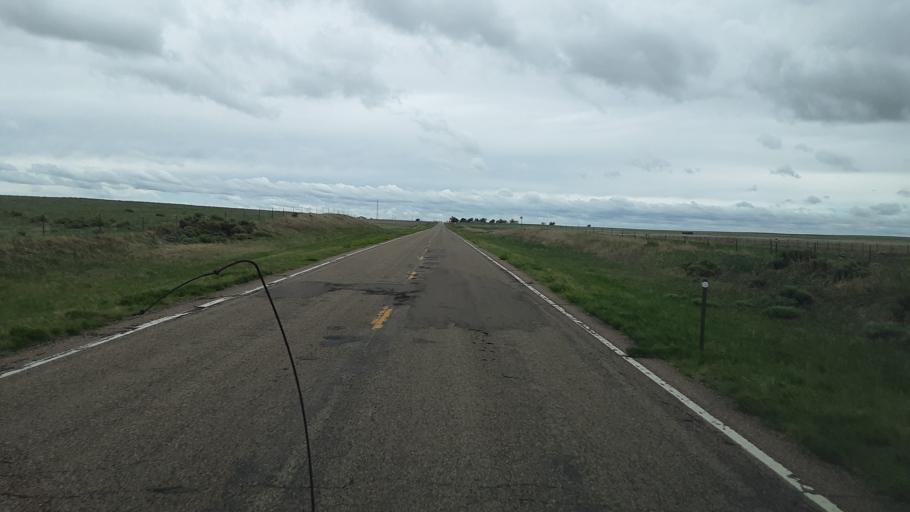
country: US
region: Colorado
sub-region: Lincoln County
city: Hugo
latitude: 38.8518
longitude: -103.6841
